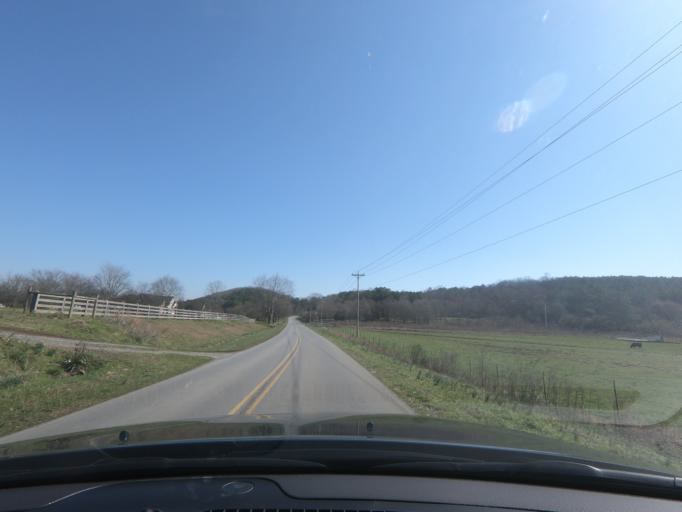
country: US
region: Georgia
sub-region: Gordon County
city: Calhoun
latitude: 34.4614
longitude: -85.0071
